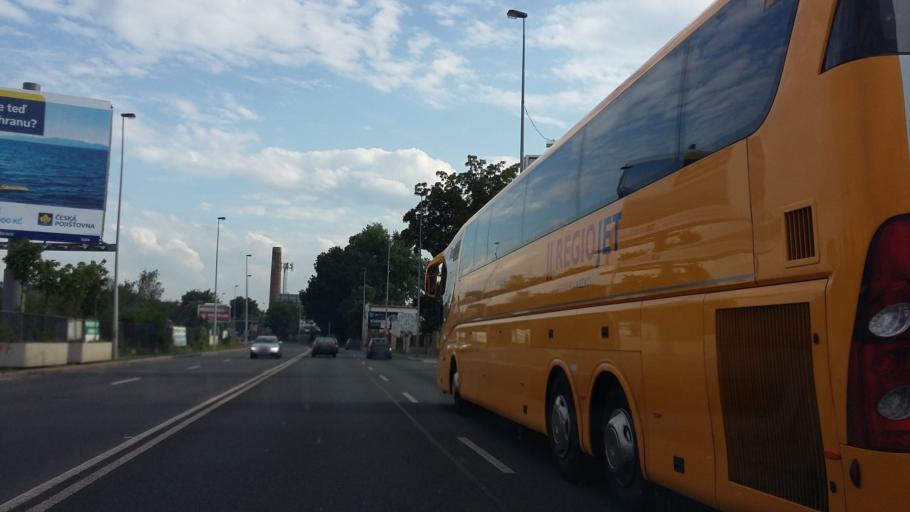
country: CZ
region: Praha
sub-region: Praha 2
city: Vysehrad
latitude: 50.0563
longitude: 14.4105
